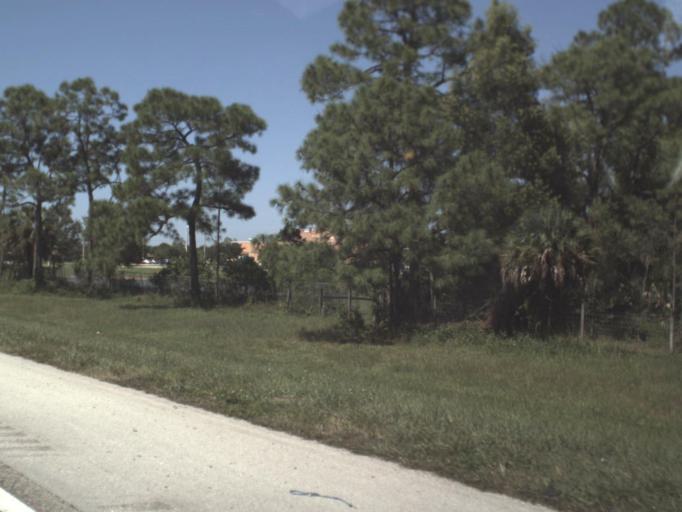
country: US
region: Florida
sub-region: Collier County
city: Golden Gate
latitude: 26.1639
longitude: -81.6994
